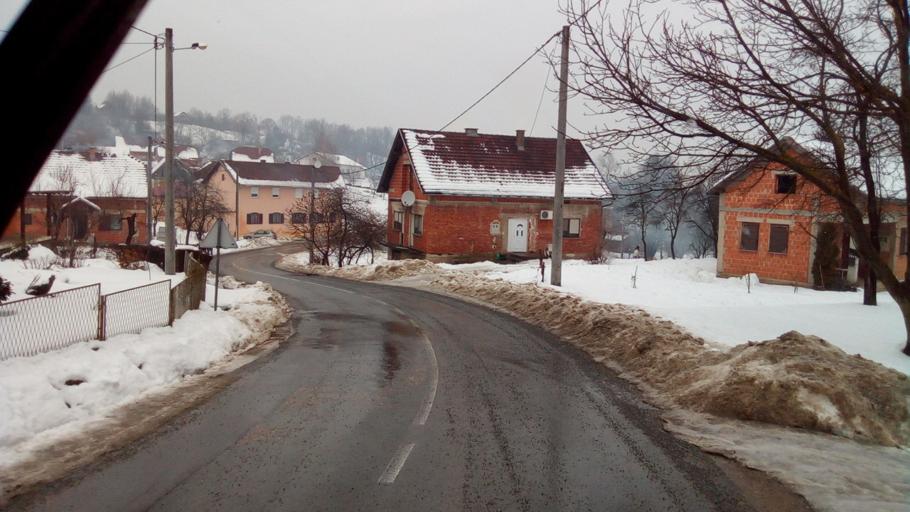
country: HR
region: Sisacko-Moslavacka
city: Petrinja
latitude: 45.3984
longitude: 16.2881
